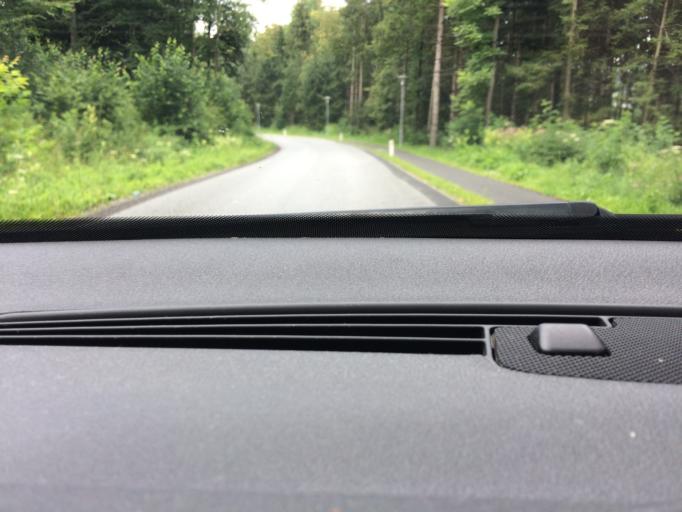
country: AT
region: Styria
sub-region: Politischer Bezirk Weiz
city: Gleisdorf
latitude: 47.0961
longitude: 15.6973
